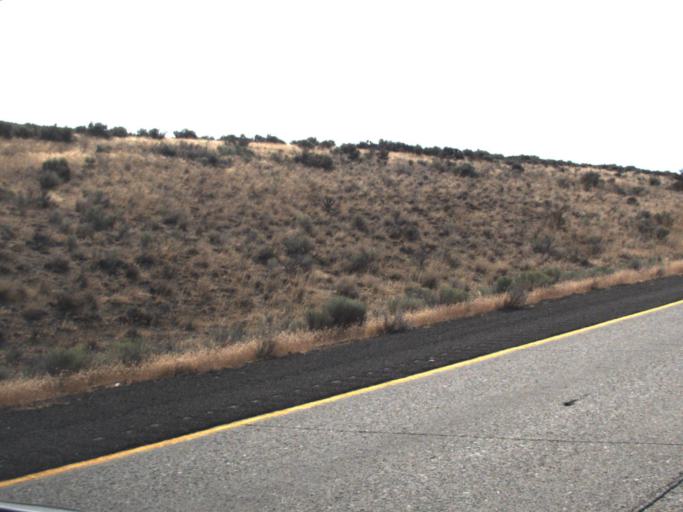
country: US
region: Washington
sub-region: Kittitas County
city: Kittitas
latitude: 46.8531
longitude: -120.3950
